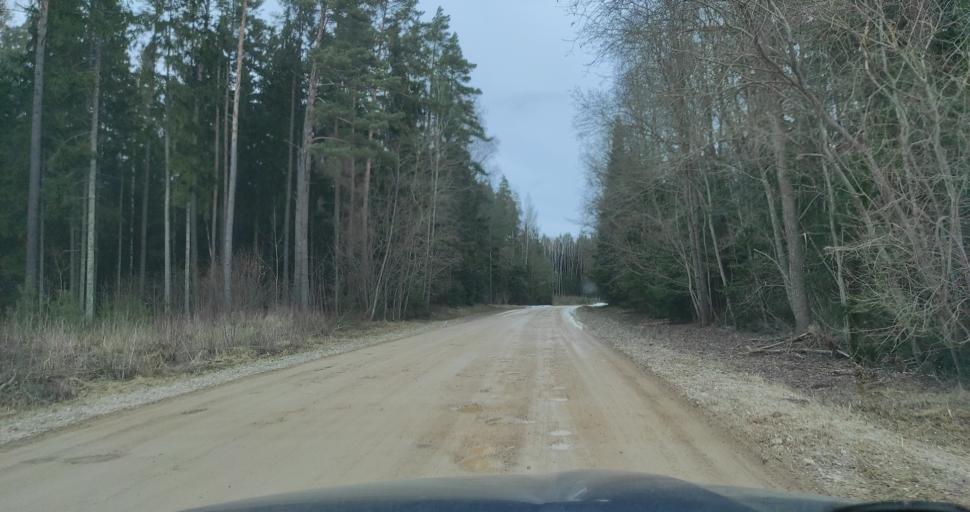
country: LV
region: Tukuma Rajons
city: Tukums
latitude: 57.0737
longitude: 23.0619
